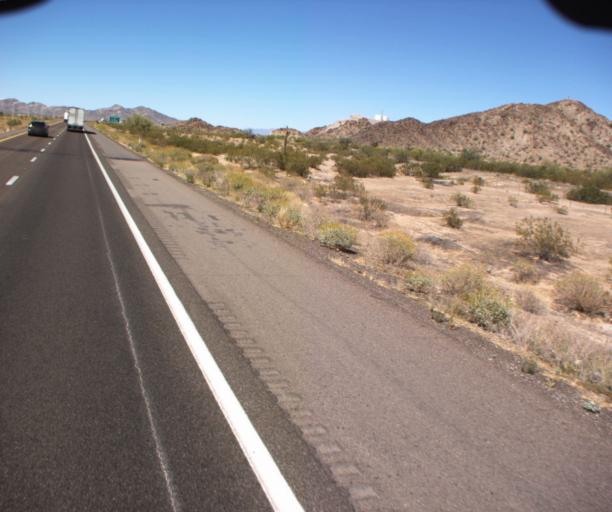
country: US
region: Arizona
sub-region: Maricopa County
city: Buckeye
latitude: 33.1831
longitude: -112.6508
